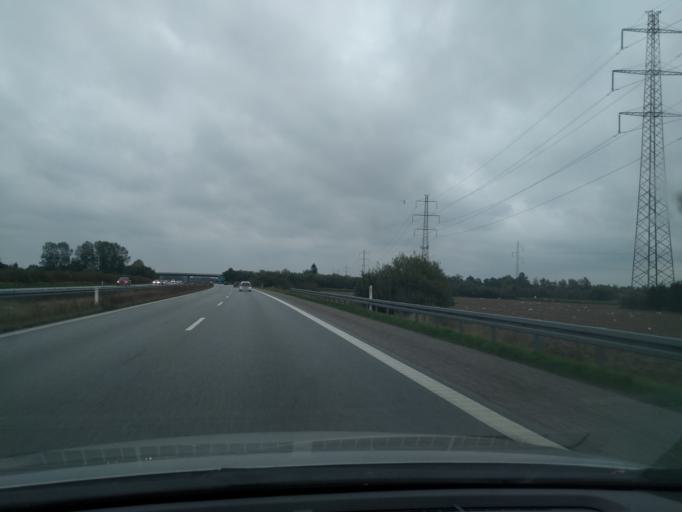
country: DK
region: Zealand
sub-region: Ringsted Kommune
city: Ringsted
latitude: 55.4564
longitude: 11.8653
